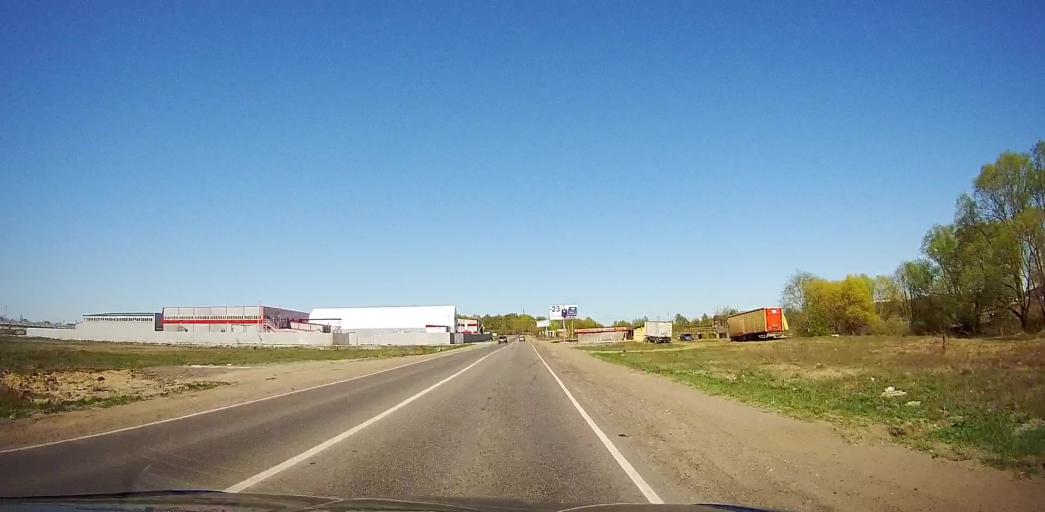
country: RU
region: Moskovskaya
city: Ramenskoye
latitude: 55.5389
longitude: 38.2802
